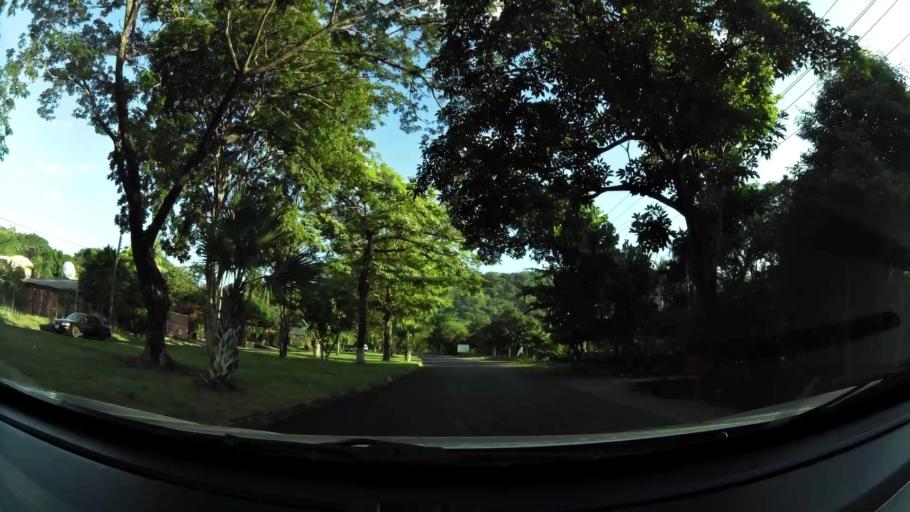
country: CR
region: Guanacaste
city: Sardinal
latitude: 10.5389
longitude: -85.6894
